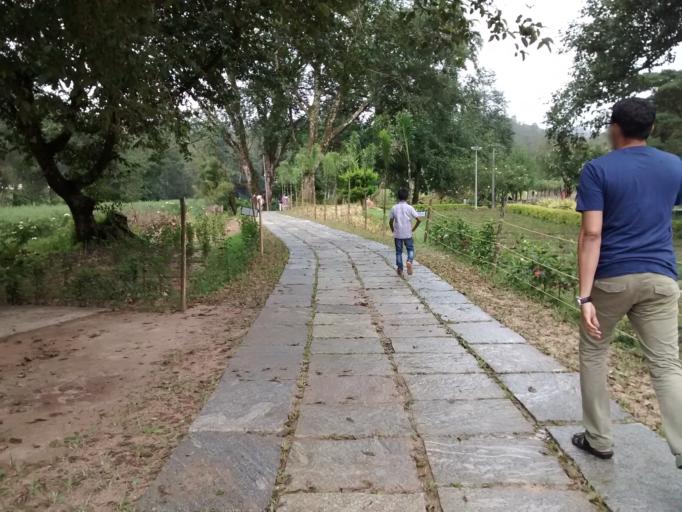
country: IN
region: Kerala
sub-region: Idukki
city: Munnar
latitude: 10.0695
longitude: 77.0636
